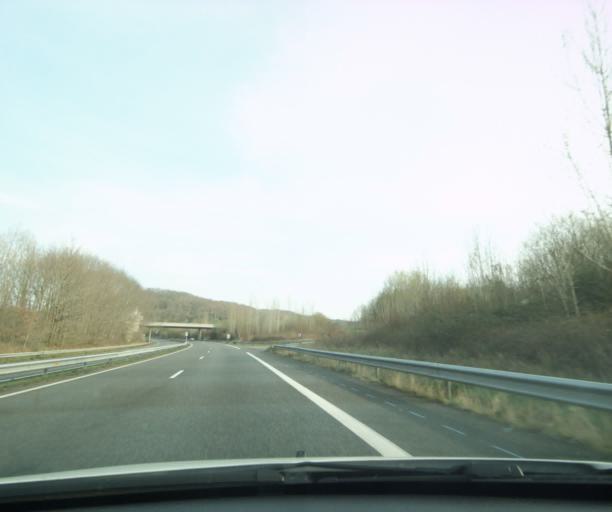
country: FR
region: Midi-Pyrenees
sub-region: Departement des Hautes-Pyrenees
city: Tournay
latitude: 43.1656
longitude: 0.2533
